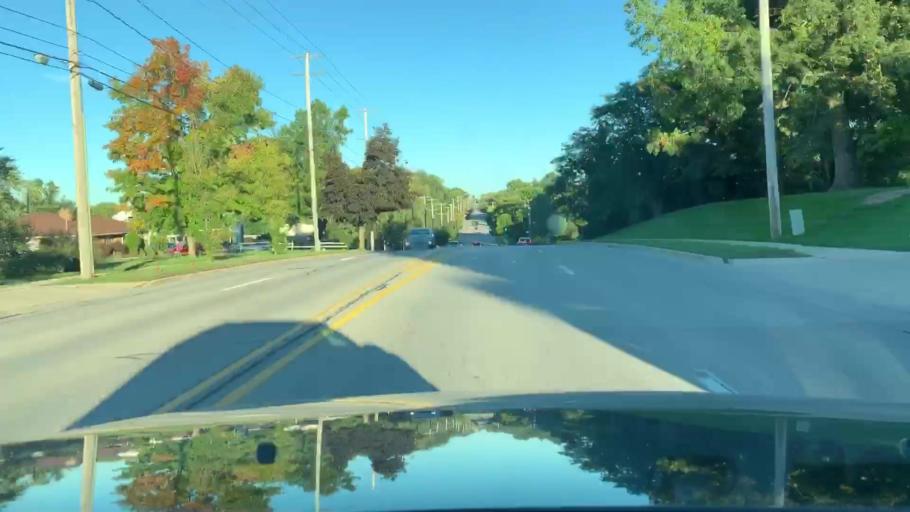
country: US
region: Michigan
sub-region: Kent County
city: East Grand Rapids
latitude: 42.9840
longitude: -85.6225
